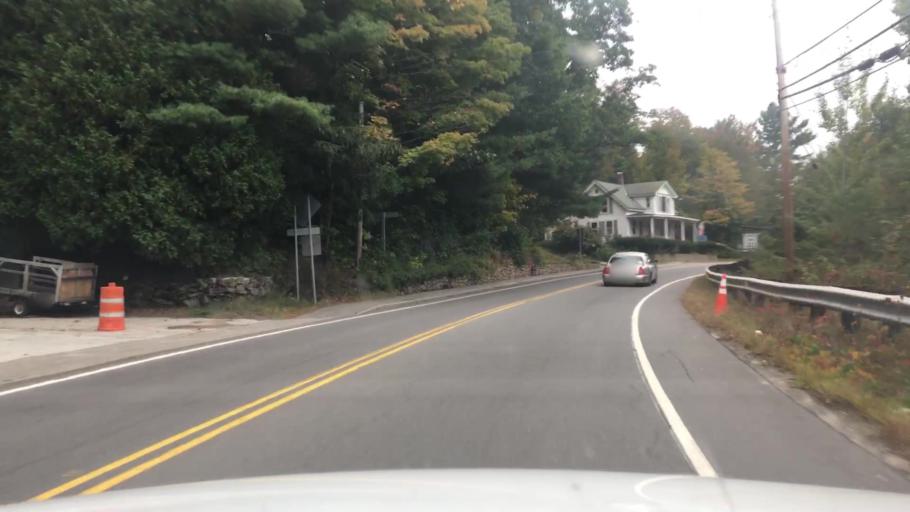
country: US
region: New Hampshire
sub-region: Strafford County
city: New Durham
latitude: 43.4700
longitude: -71.2324
